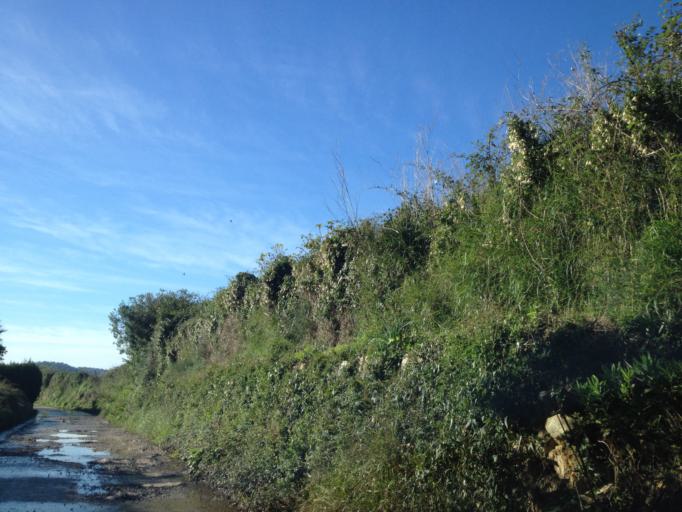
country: ES
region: Balearic Islands
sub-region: Illes Balears
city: Sineu
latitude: 39.6442
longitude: 3.0328
